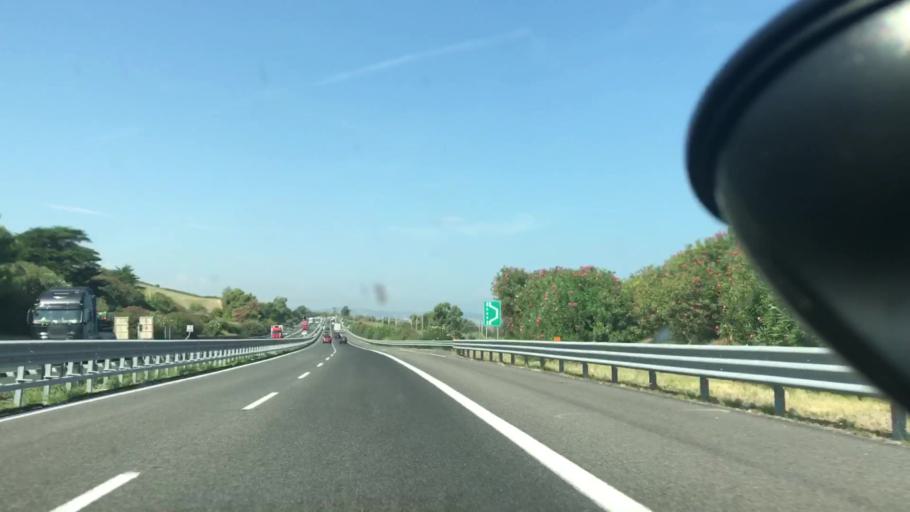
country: IT
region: Molise
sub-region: Provincia di Campobasso
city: Petacciato
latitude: 42.0257
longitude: 14.8805
